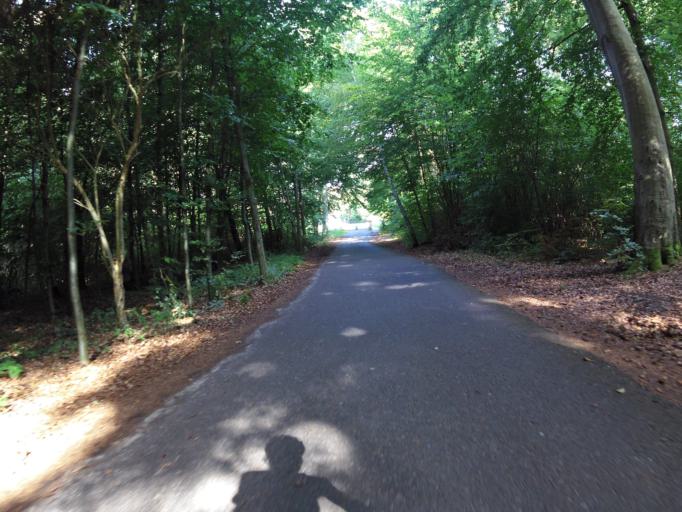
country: DE
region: Mecklenburg-Vorpommern
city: Seebad Bansin
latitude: 53.9929
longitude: 14.1114
